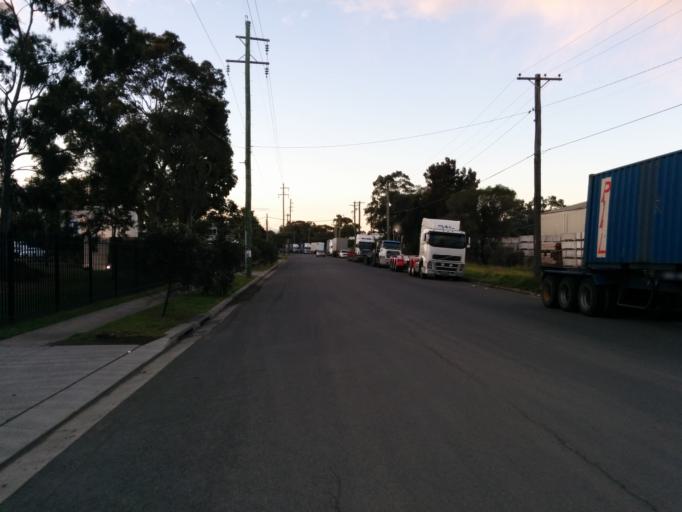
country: AU
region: New South Wales
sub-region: Fairfield
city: Fairfield East
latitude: -33.8650
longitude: 150.9633
